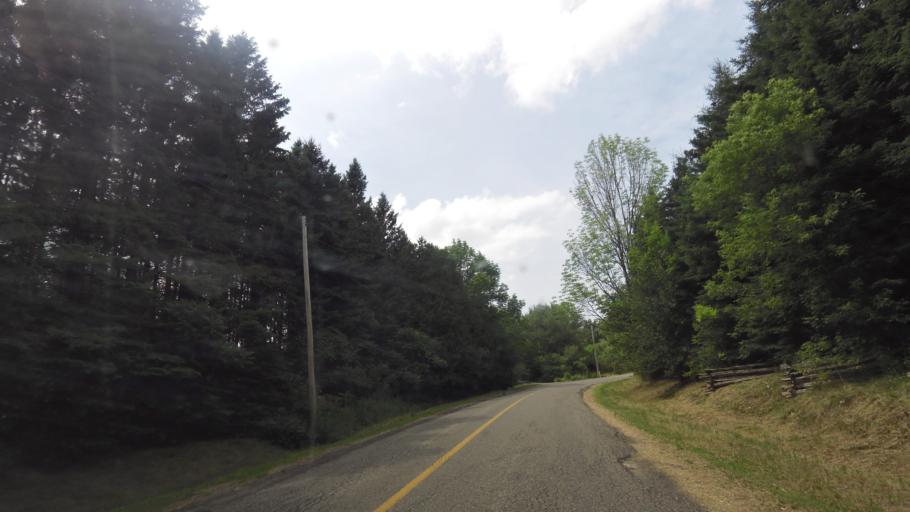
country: CA
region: Ontario
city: Orangeville
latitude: 43.8683
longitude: -79.9110
